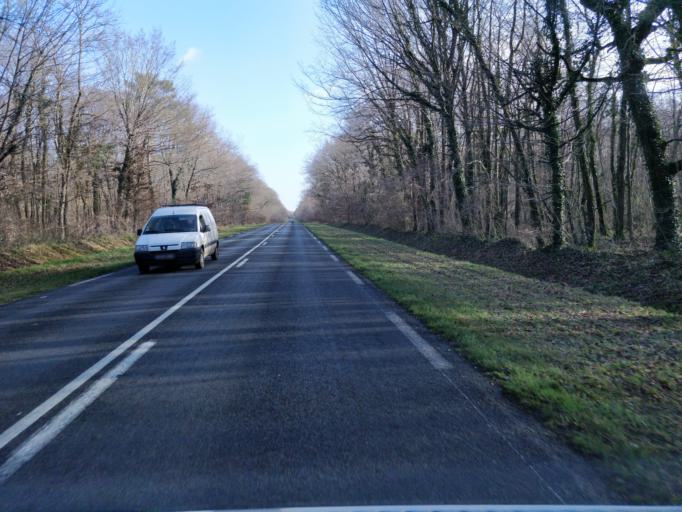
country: FR
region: Ile-de-France
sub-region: Departement de Seine-et-Marne
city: Souppes-sur-Loing
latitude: 48.2447
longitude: 2.7859
